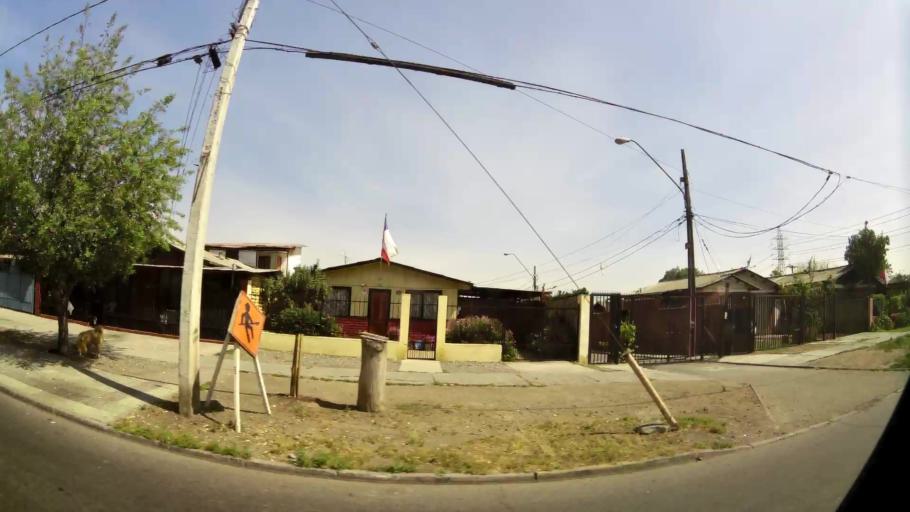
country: CL
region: Santiago Metropolitan
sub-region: Provincia de Santiago
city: Lo Prado
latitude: -33.4089
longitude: -70.7077
